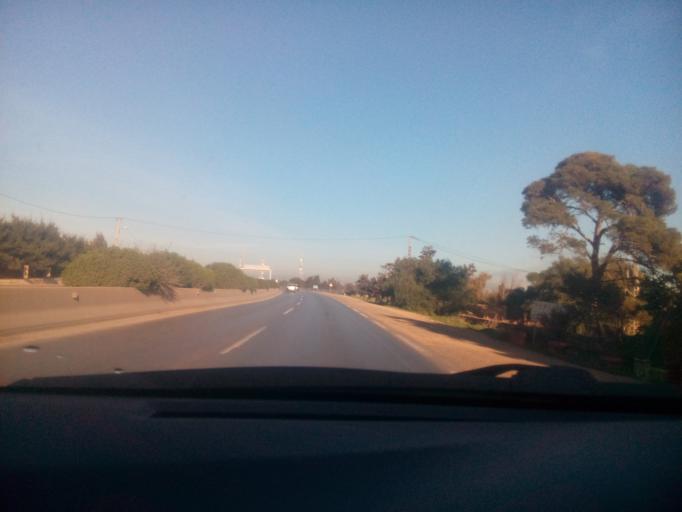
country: DZ
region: Oran
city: Bir el Djir
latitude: 35.7494
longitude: -0.4887
